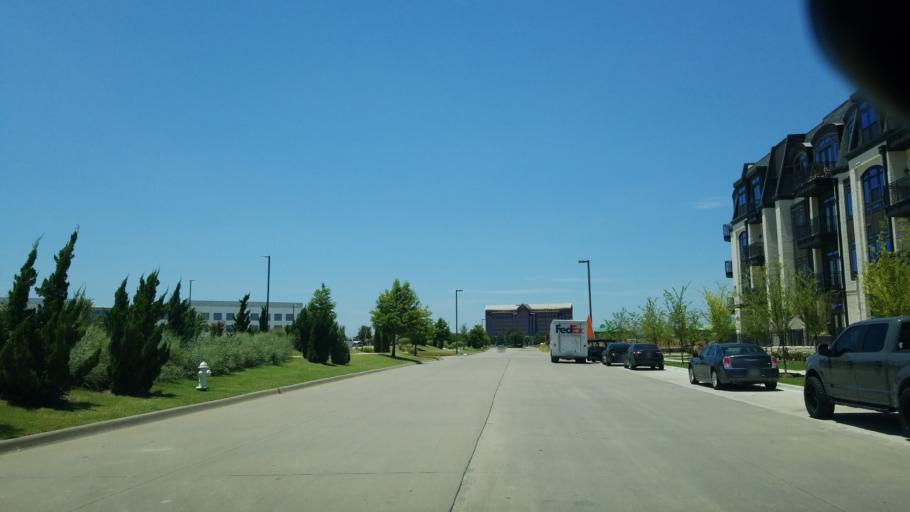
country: US
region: Texas
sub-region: Dallas County
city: Farmers Branch
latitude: 32.9173
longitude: -96.9113
